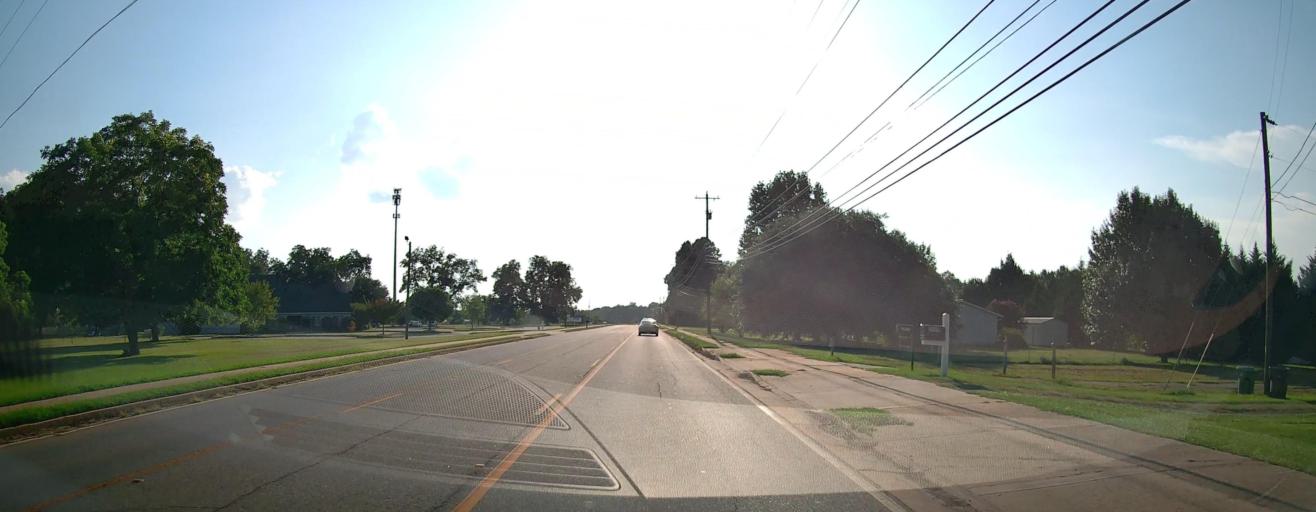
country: US
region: Georgia
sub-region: Houston County
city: Perry
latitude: 32.5062
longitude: -83.6545
